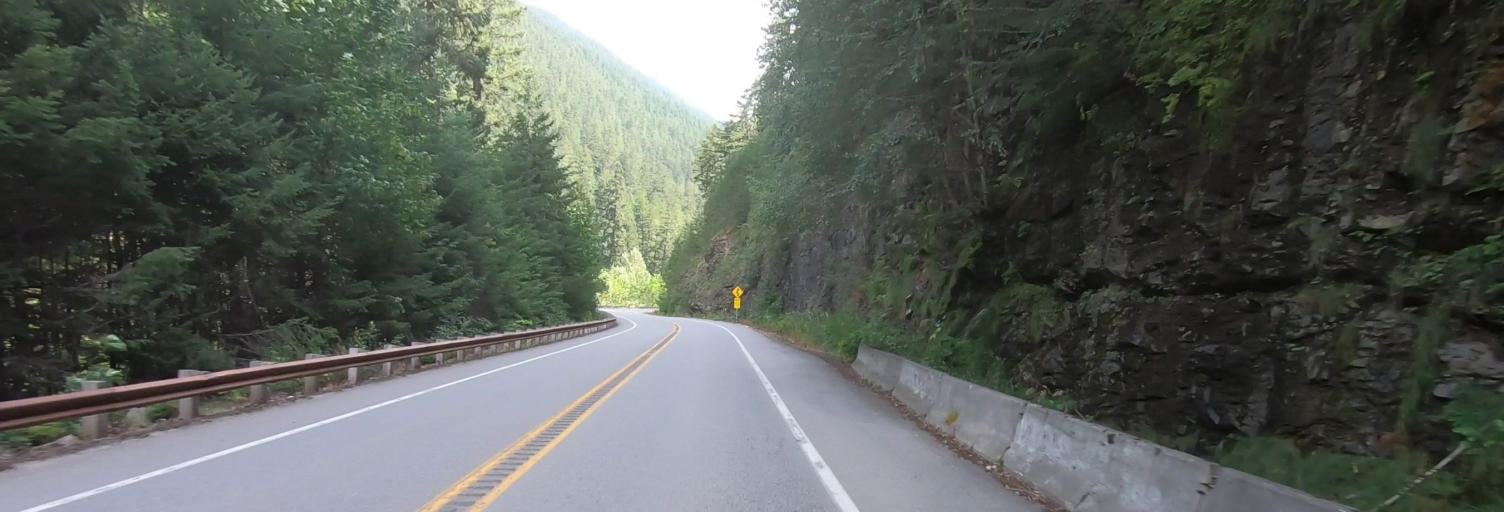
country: US
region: Washington
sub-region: Snohomish County
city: Darrington
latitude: 48.6951
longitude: -120.9115
